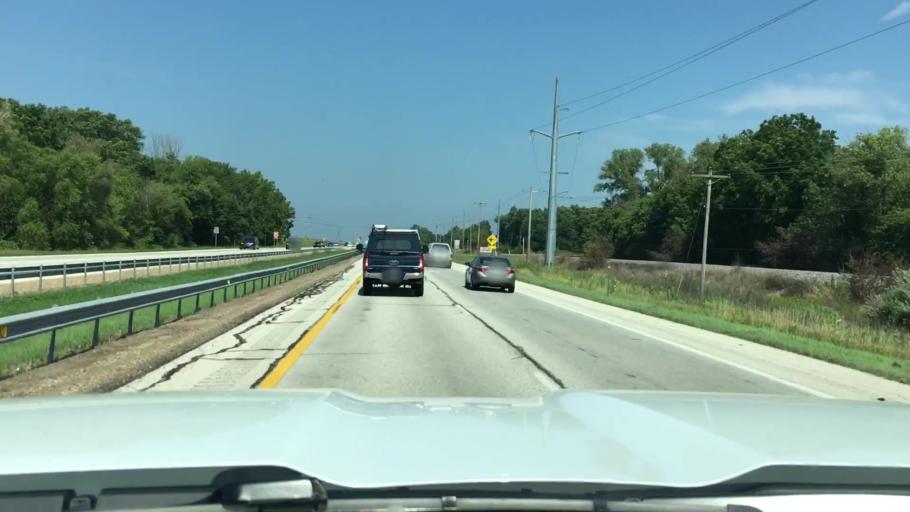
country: US
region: Michigan
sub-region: Kalamazoo County
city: Schoolcraft
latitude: 42.0609
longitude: -85.6360
